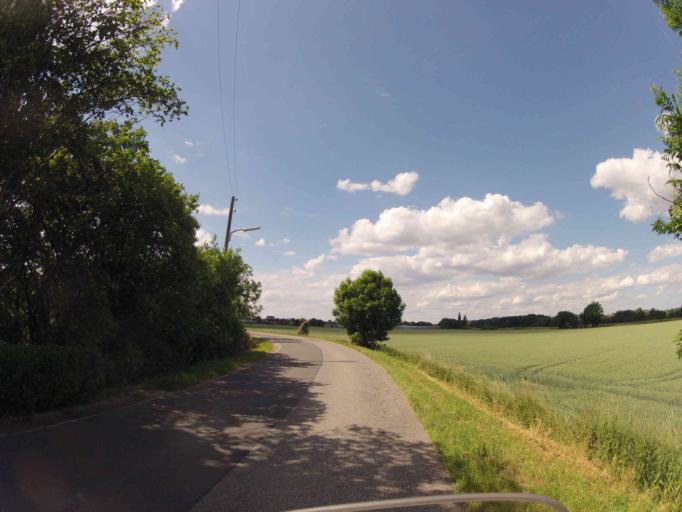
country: DE
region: Lower Saxony
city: Stelle
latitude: 53.4675
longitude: 10.1108
